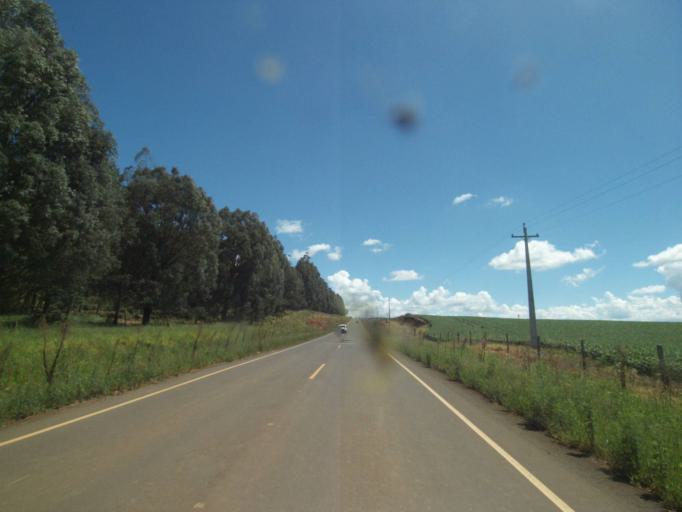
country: BR
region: Parana
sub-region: Pinhao
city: Pinhao
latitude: -25.8291
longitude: -52.0188
